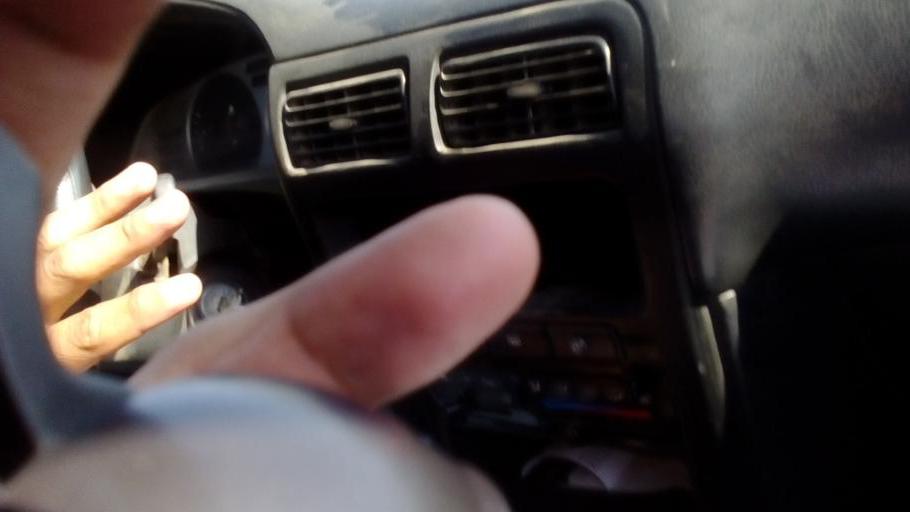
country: MX
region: Guanajuato
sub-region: Leon
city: Medina
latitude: 21.1377
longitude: -101.6115
